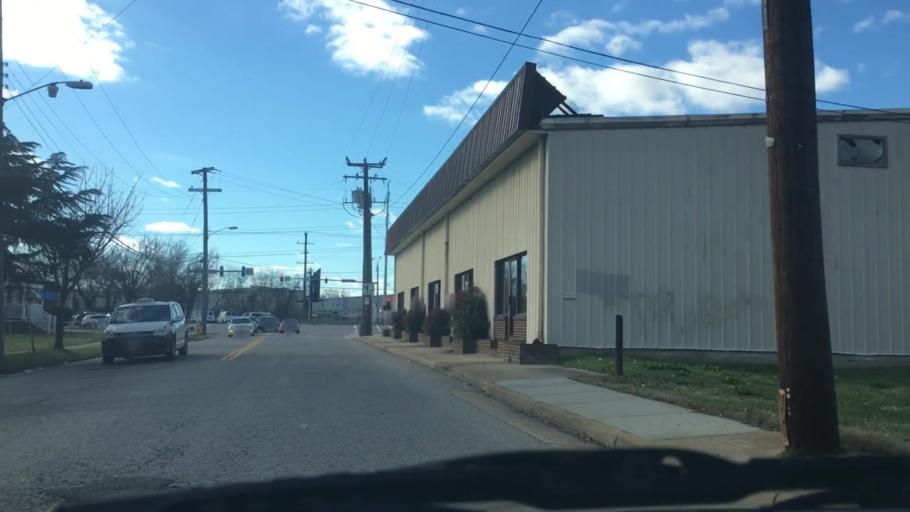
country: US
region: Virginia
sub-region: City of Norfolk
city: Norfolk
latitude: 36.9018
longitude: -76.2553
